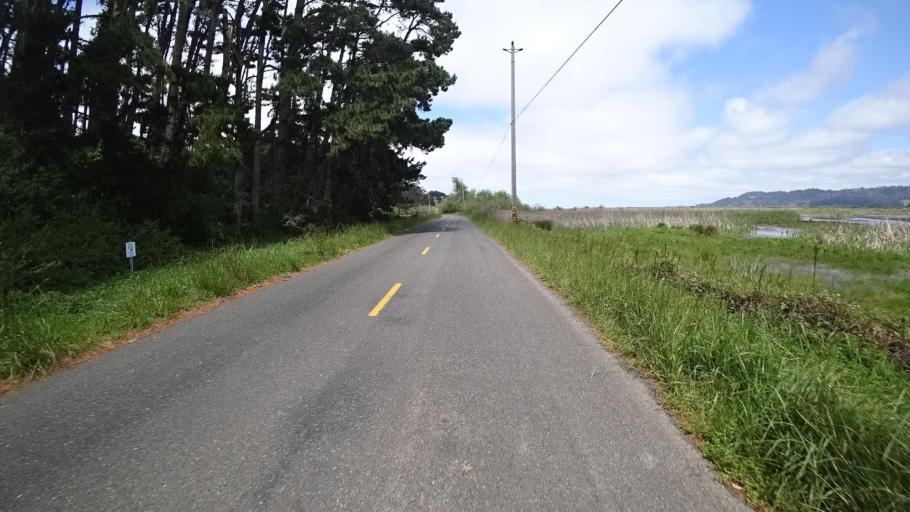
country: US
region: California
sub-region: Humboldt County
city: Humboldt Hill
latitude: 40.6817
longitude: -124.2302
